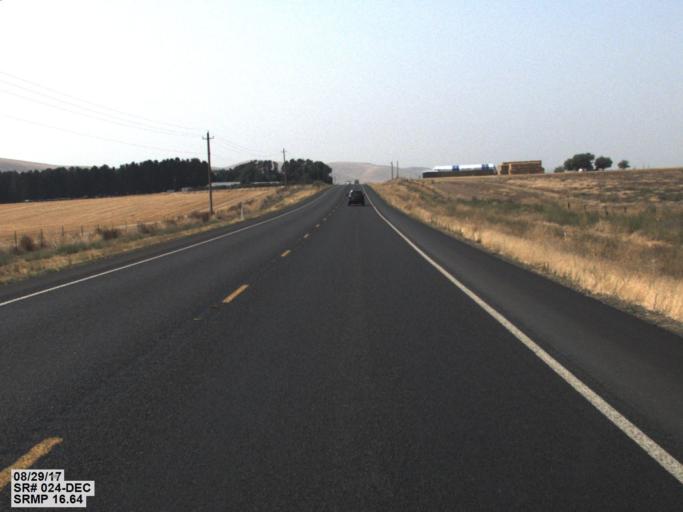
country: US
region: Washington
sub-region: Yakima County
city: Zillah
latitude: 46.5058
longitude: -120.1600
